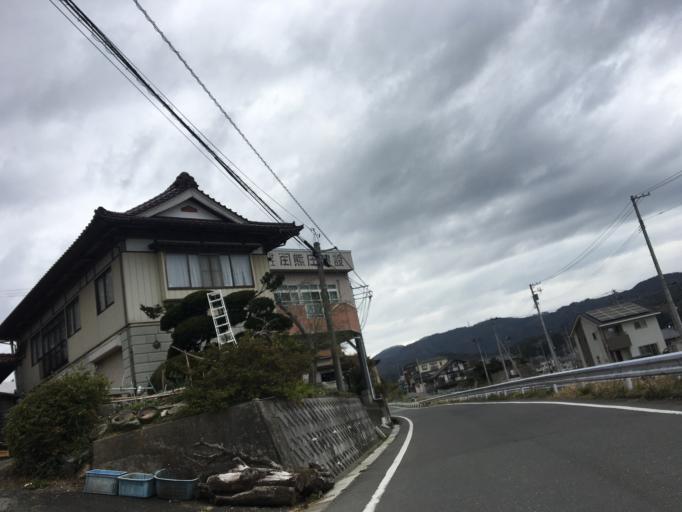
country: JP
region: Iwate
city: Ofunato
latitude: 38.9167
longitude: 141.5800
